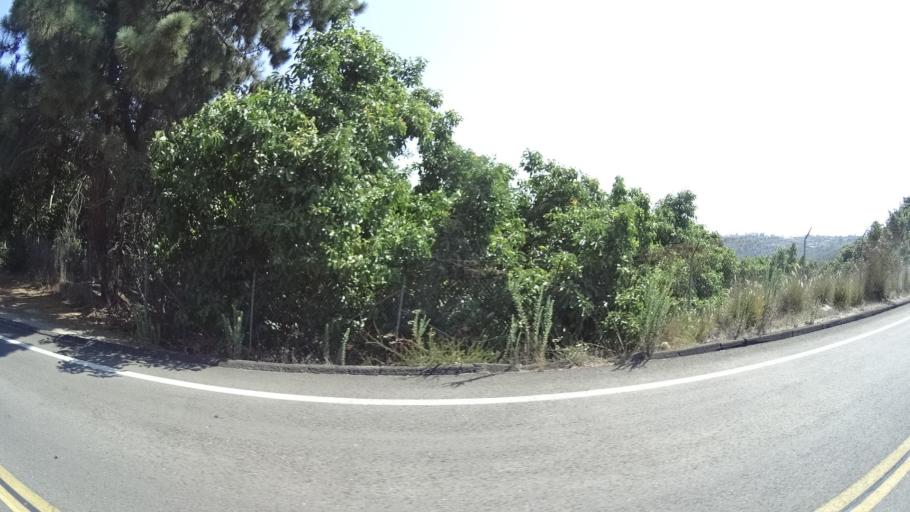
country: US
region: California
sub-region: San Diego County
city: Valley Center
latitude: 33.3028
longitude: -117.0132
